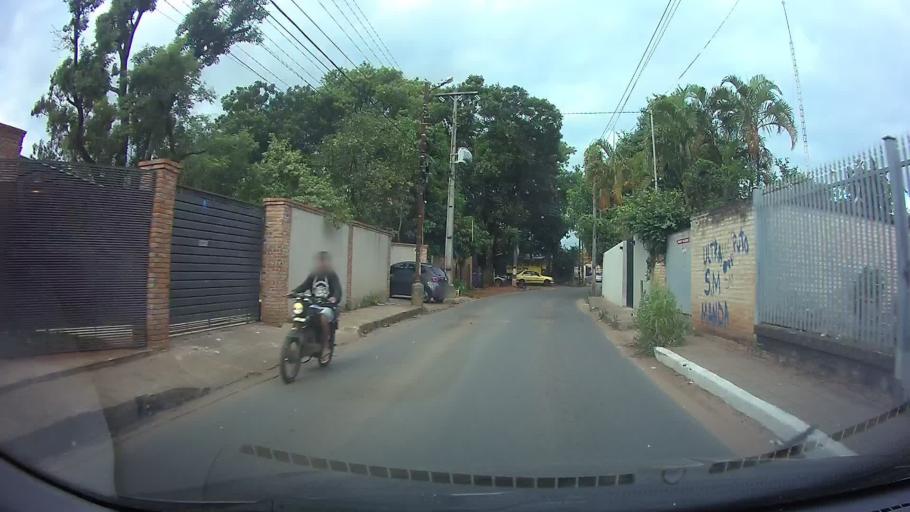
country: PY
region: Central
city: Fernando de la Mora
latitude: -25.3034
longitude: -57.5225
